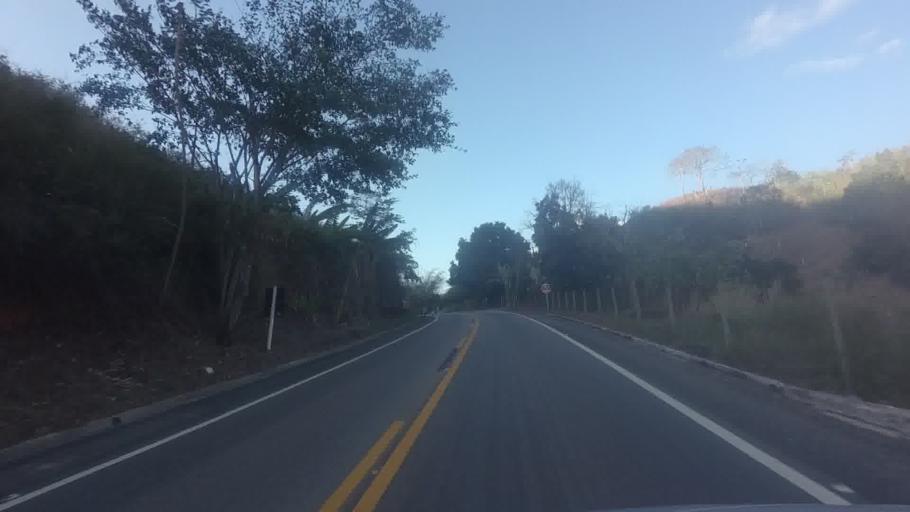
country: BR
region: Espirito Santo
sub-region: Cachoeiro De Itapemirim
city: Cachoeiro de Itapemirim
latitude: -20.8488
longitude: -41.2427
